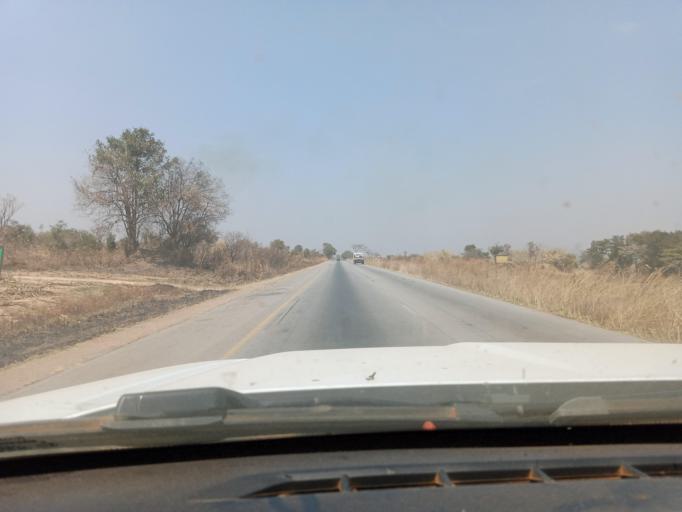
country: ZM
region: Copperbelt
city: Luanshya
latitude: -12.9982
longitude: 28.4218
